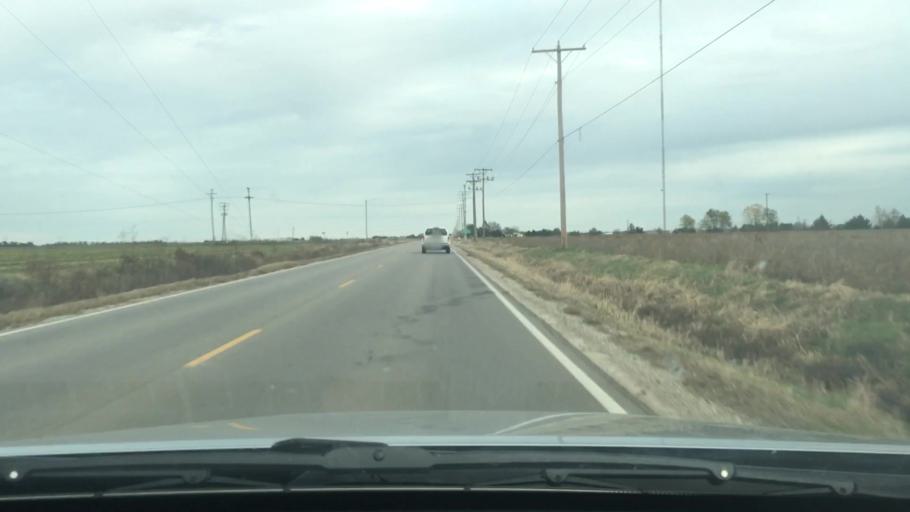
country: US
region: Kansas
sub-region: Sedgwick County
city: Colwich
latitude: 37.7796
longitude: -97.5205
